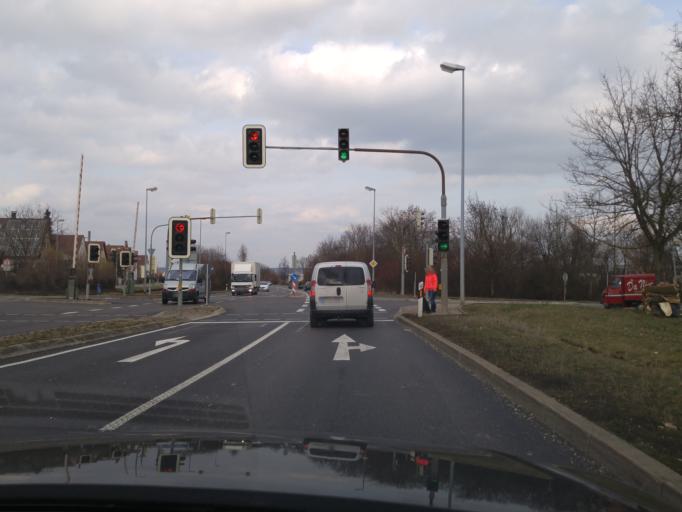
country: DE
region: Baden-Wuerttemberg
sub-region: Regierungsbezirk Stuttgart
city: Dettingen unter Teck
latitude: 48.6126
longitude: 9.4547
